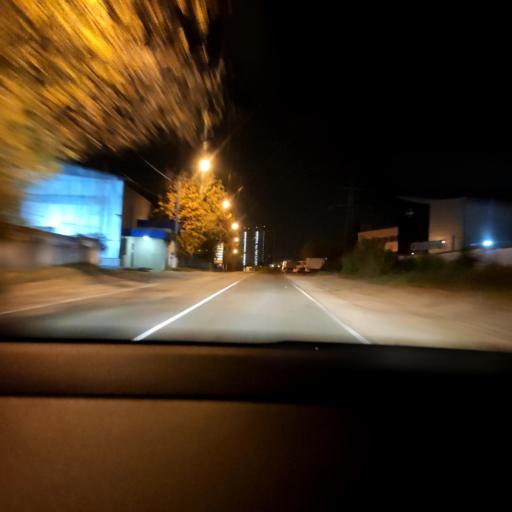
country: RU
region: Moskovskaya
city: Bolshevo
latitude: 55.9395
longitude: 37.8301
